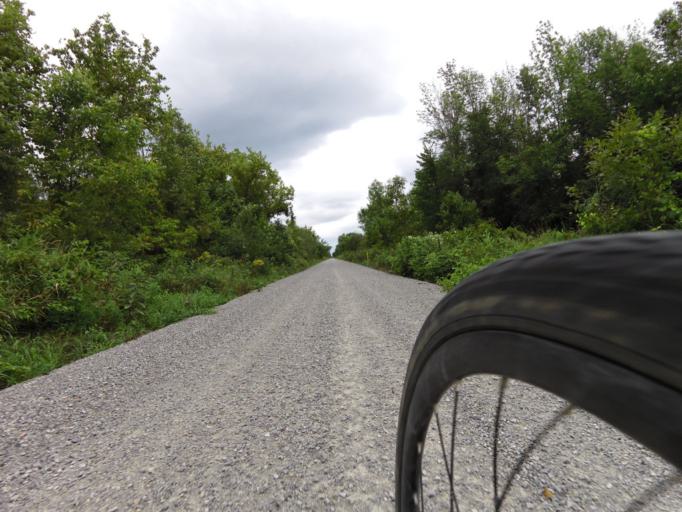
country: CA
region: Ontario
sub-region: Lanark County
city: Smiths Falls
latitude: 44.9281
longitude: -76.0330
